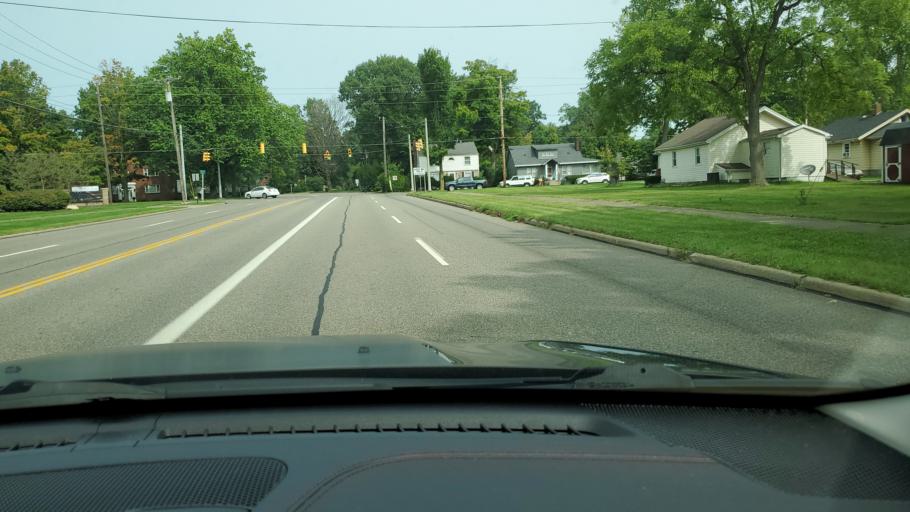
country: US
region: Ohio
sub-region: Mahoning County
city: Boardman
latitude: 41.0457
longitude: -80.6722
